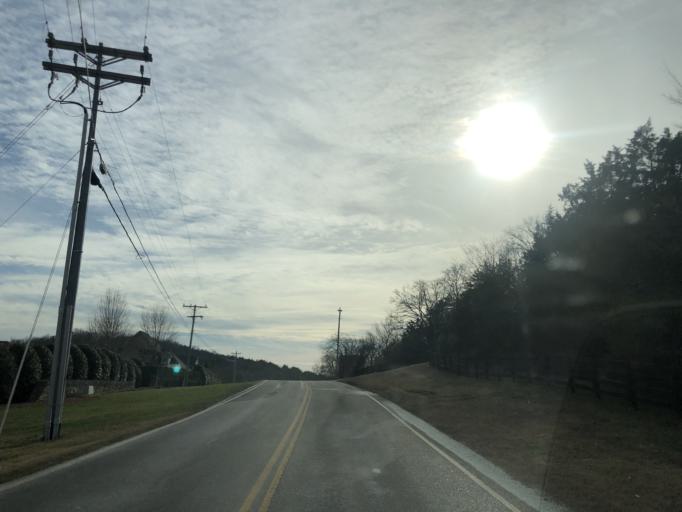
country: US
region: Tennessee
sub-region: Williamson County
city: Franklin
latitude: 35.9341
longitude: -86.9065
